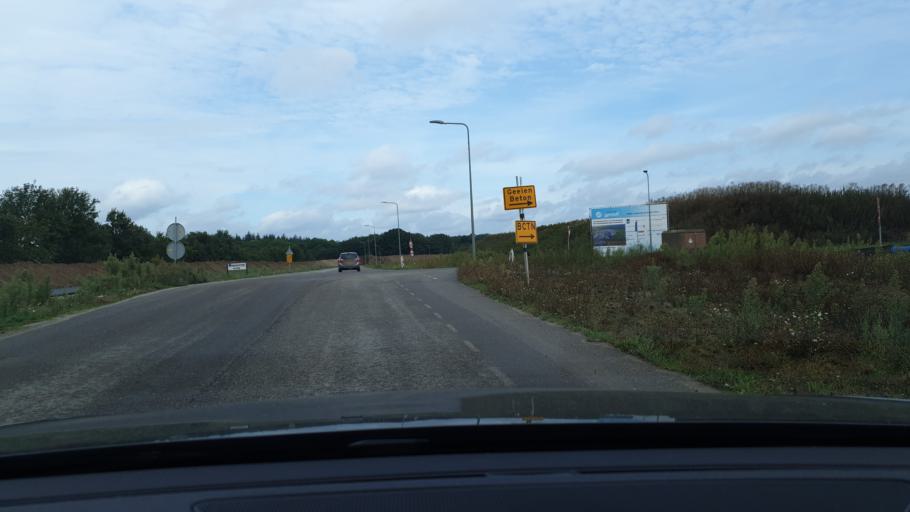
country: NL
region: Limburg
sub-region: Gemeente Bergen
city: Wellerlooi
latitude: 51.5415
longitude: 6.0697
